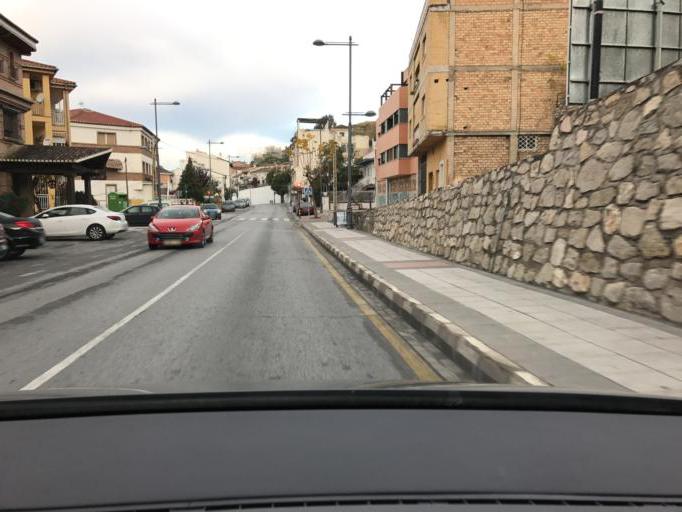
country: ES
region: Andalusia
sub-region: Provincia de Granada
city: Cenes de la Vega
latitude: 37.1580
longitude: -3.5317
